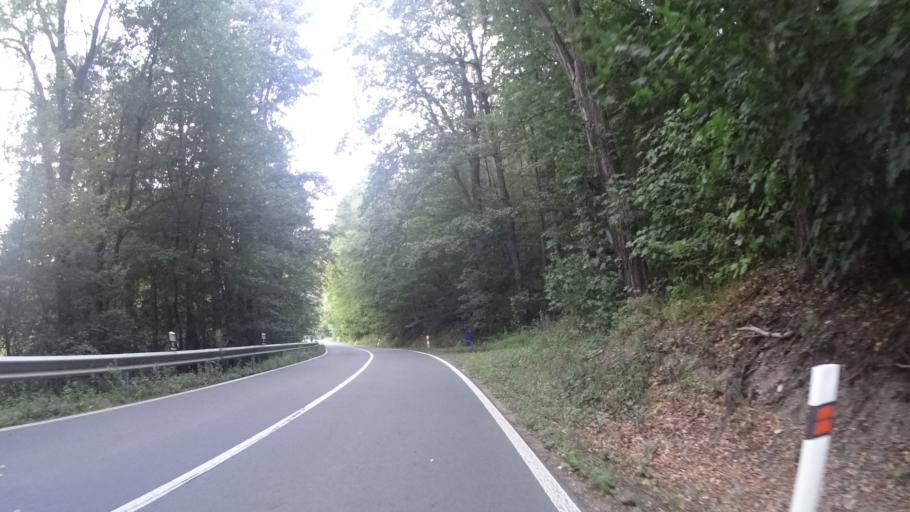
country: CZ
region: Olomoucky
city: Stity
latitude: 49.8657
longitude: 16.7369
